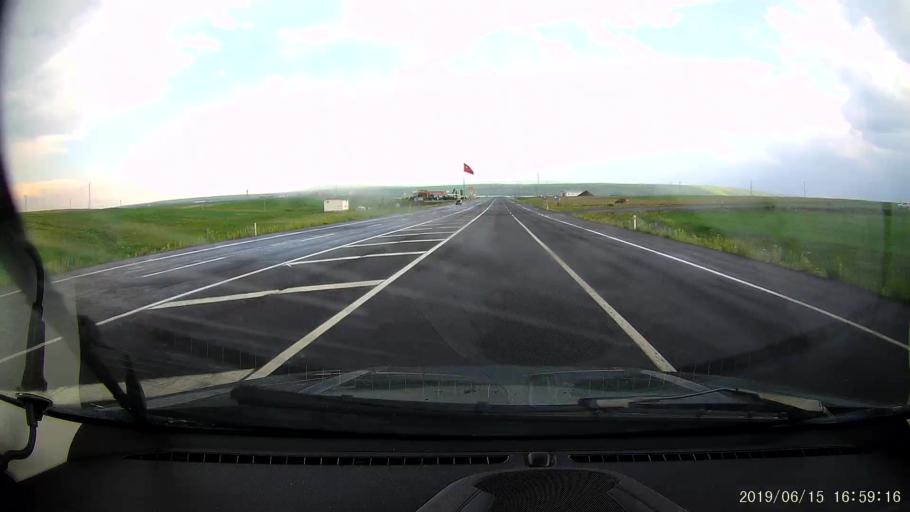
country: TR
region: Kars
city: Susuz
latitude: 40.7540
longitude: 43.1495
